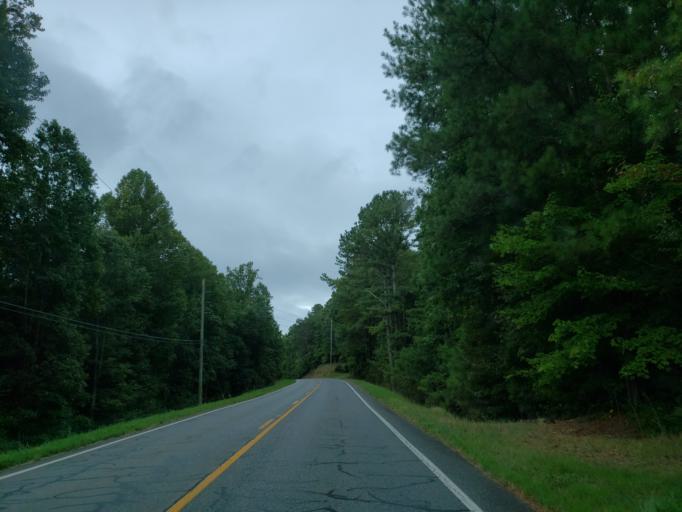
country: US
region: Georgia
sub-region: Gilmer County
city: Ellijay
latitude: 34.6340
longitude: -84.5787
